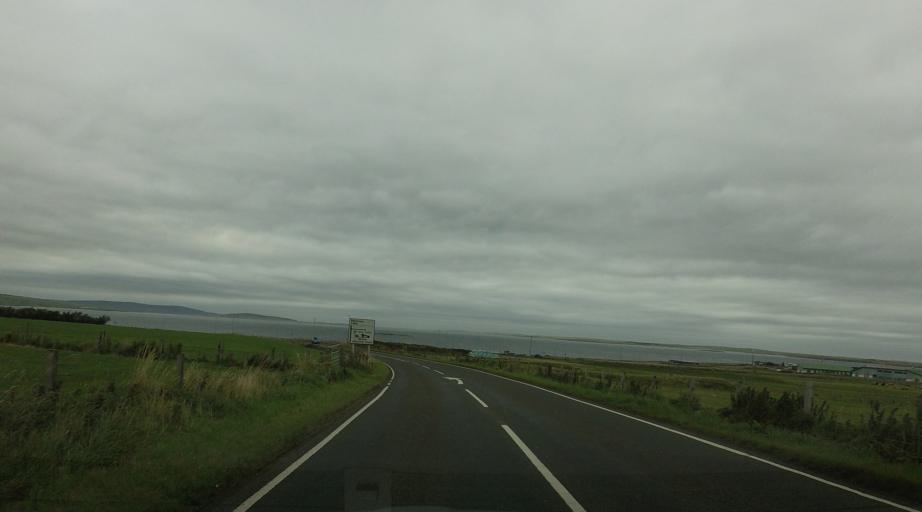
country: GB
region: Scotland
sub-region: Orkney Islands
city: Orkney
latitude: 58.9970
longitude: -2.9922
